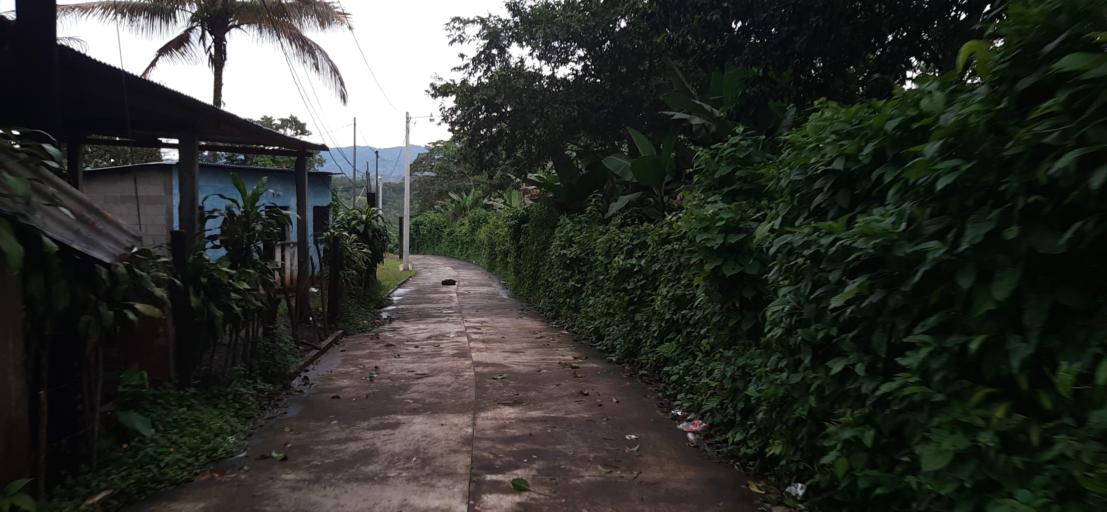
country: GT
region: Retalhuleu
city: San Felipe
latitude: 14.6276
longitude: -91.5978
